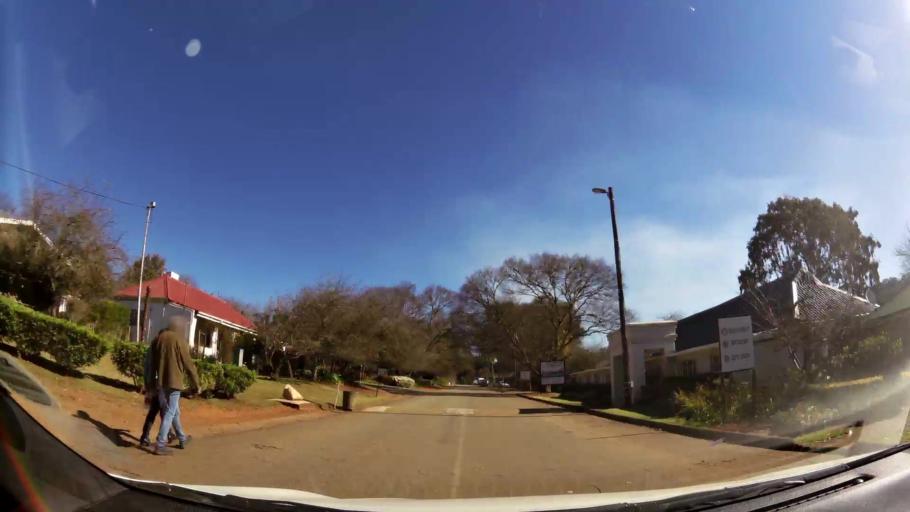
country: ZA
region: Limpopo
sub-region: Capricorn District Municipality
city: Mankoeng
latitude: -23.9425
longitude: 29.9399
